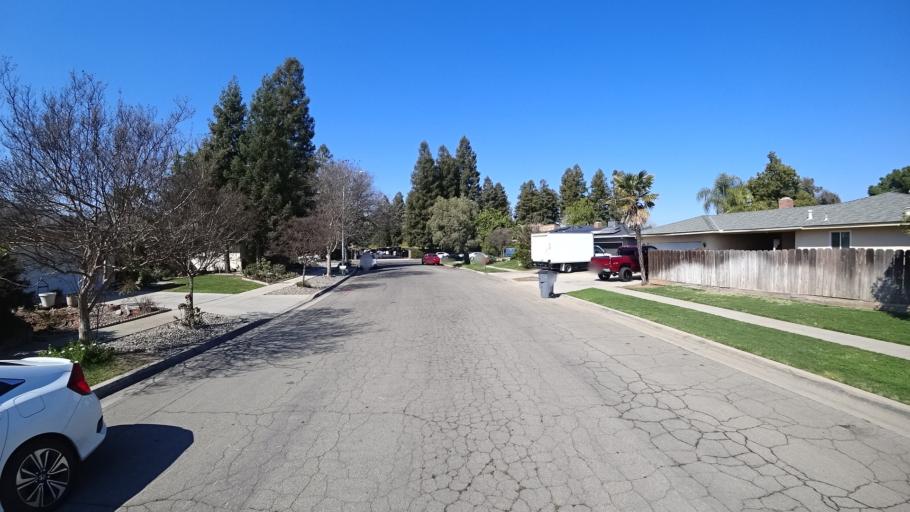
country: US
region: California
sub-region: Fresno County
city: Clovis
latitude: 36.8367
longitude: -119.7399
